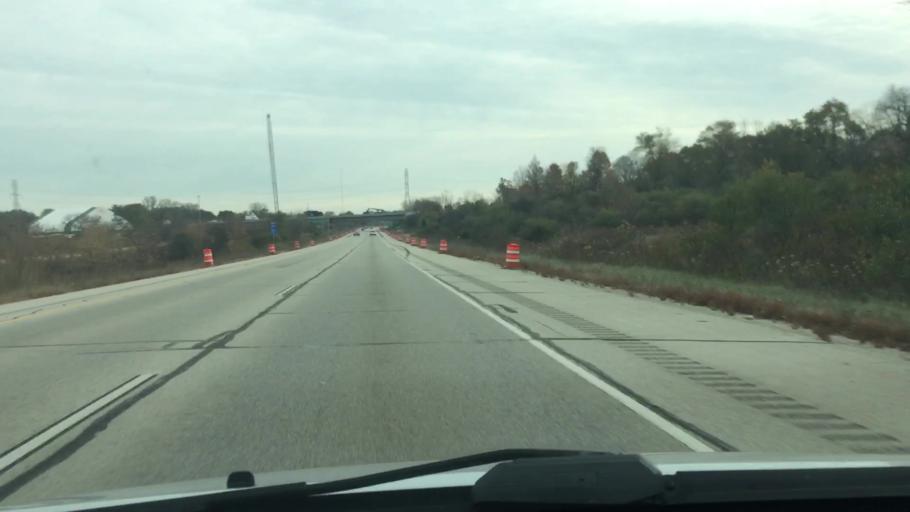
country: US
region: Wisconsin
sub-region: Waukesha County
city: Big Bend
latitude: 42.9221
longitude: -88.1930
